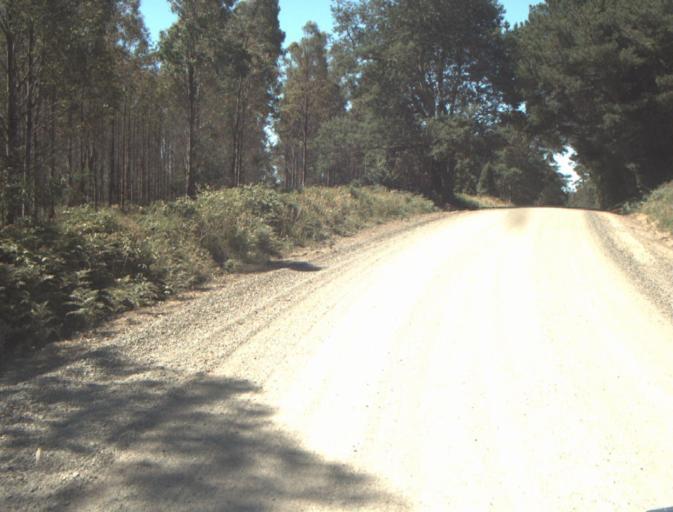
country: AU
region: Tasmania
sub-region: Dorset
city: Scottsdale
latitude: -41.3395
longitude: 147.4308
